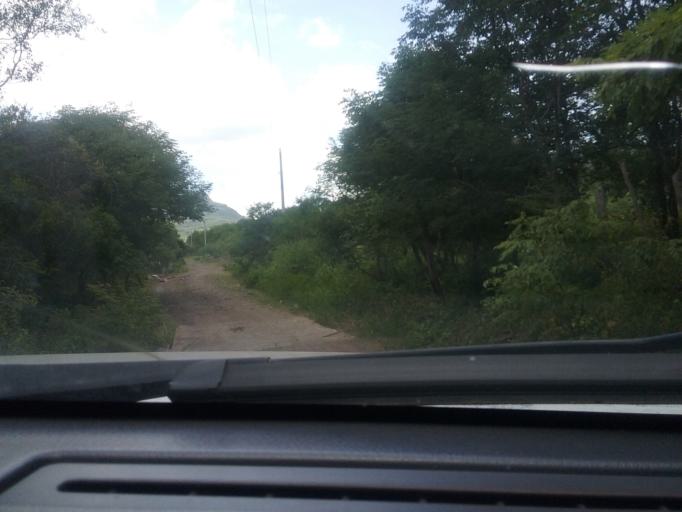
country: NI
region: Matagalpa
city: Terrabona
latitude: 12.6614
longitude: -85.9870
